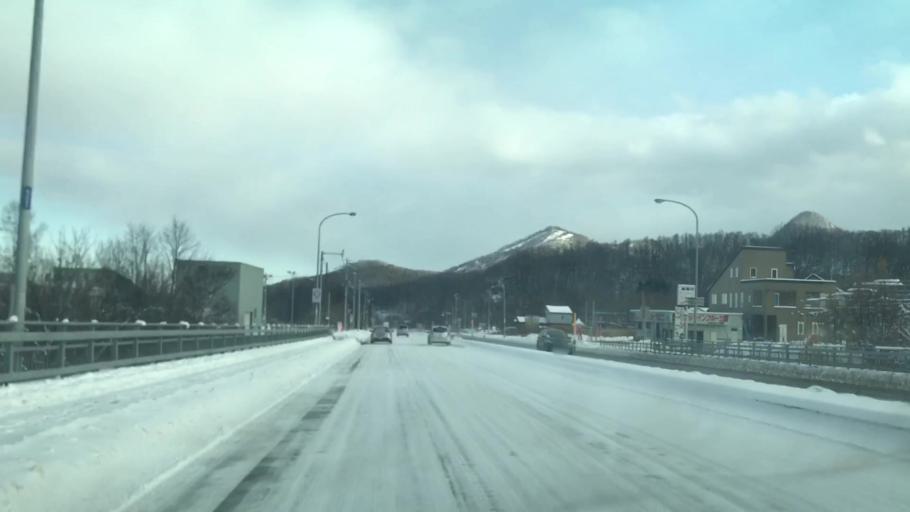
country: JP
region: Hokkaido
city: Sapporo
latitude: 42.9569
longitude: 141.2358
